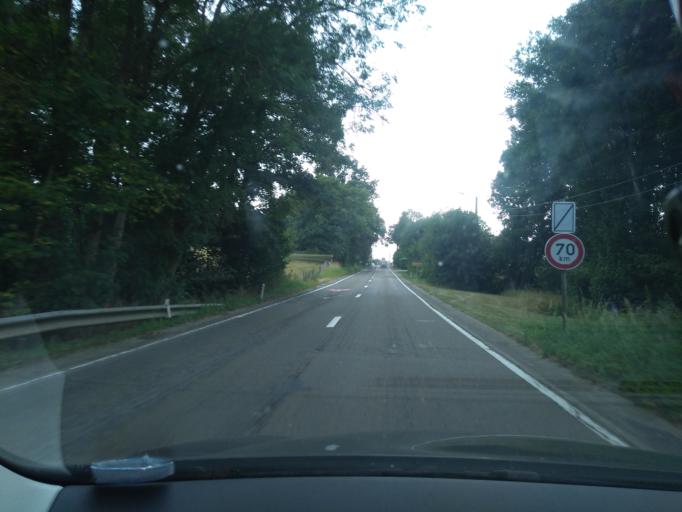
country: BE
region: Wallonia
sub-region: Province du Luxembourg
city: Sainte-Ode
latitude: 50.0365
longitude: 5.5470
